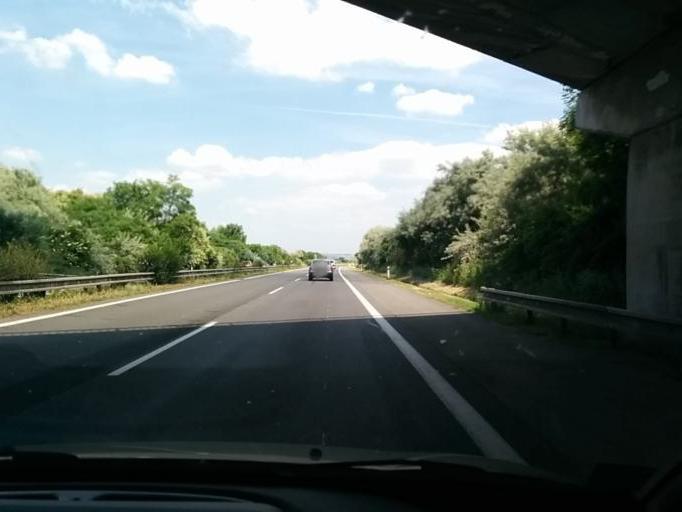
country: SK
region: Trnavsky
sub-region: Okres Trnava
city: Trnava
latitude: 48.3547
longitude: 17.6643
